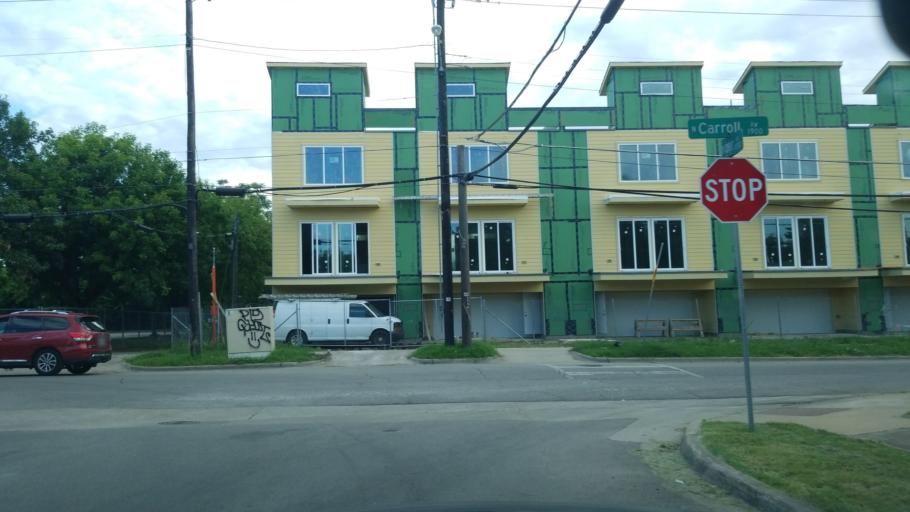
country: US
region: Texas
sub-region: Dallas County
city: Highland Park
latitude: 32.8041
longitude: -96.7817
